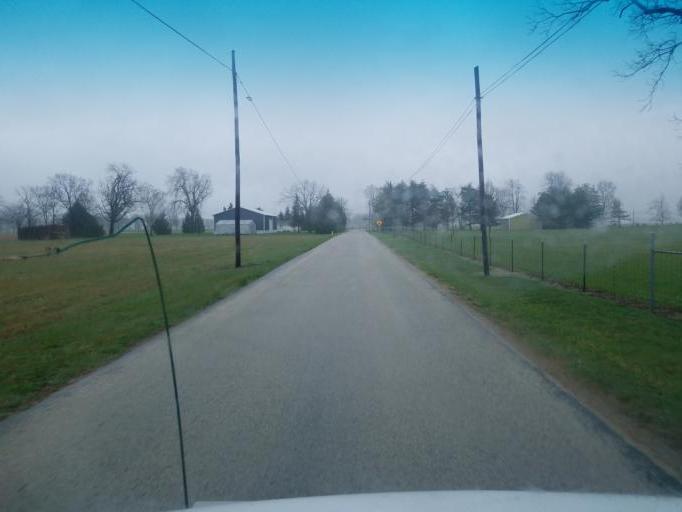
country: US
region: Ohio
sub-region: Wood County
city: North Baltimore
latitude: 41.2421
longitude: -83.6308
